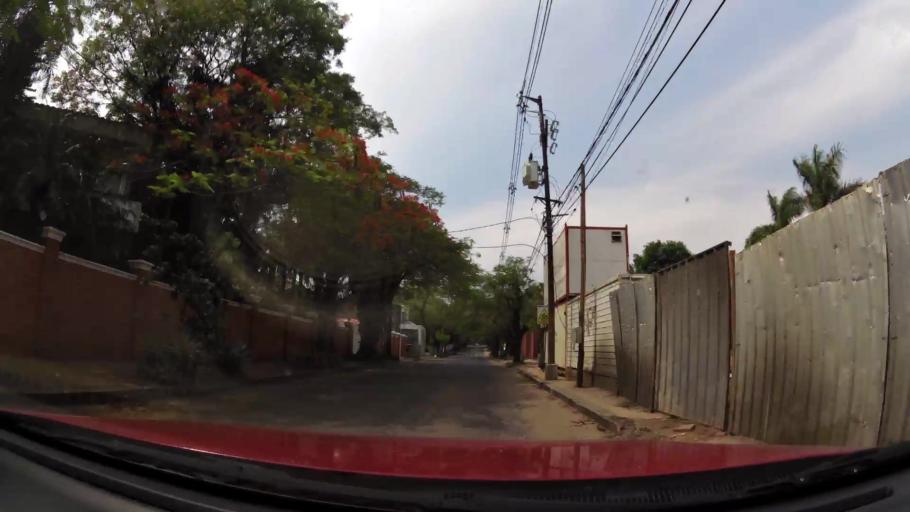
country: PY
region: Asuncion
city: Asuncion
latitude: -25.2893
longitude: -57.5859
